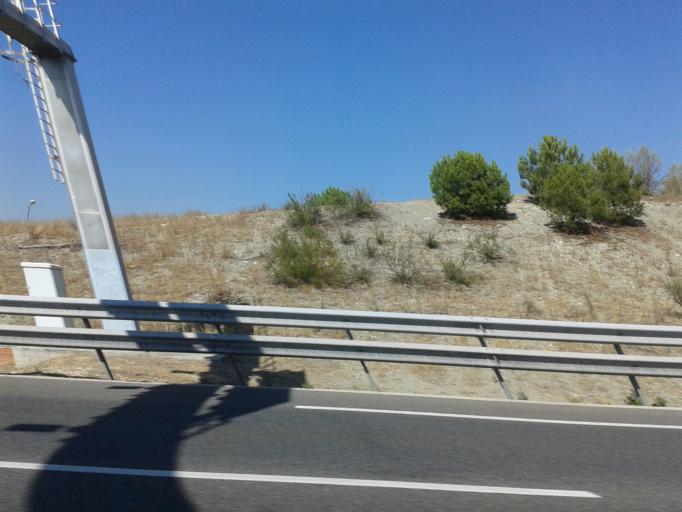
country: ES
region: Madrid
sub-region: Provincia de Madrid
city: Torrejon de Ardoz
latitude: 40.4558
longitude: -3.5067
